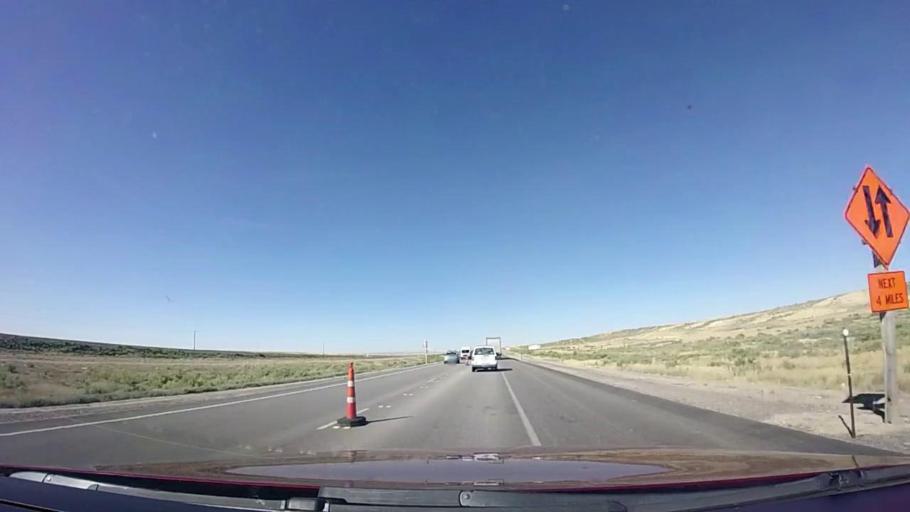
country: US
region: Wyoming
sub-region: Carbon County
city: Rawlins
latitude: 41.7014
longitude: -107.9080
